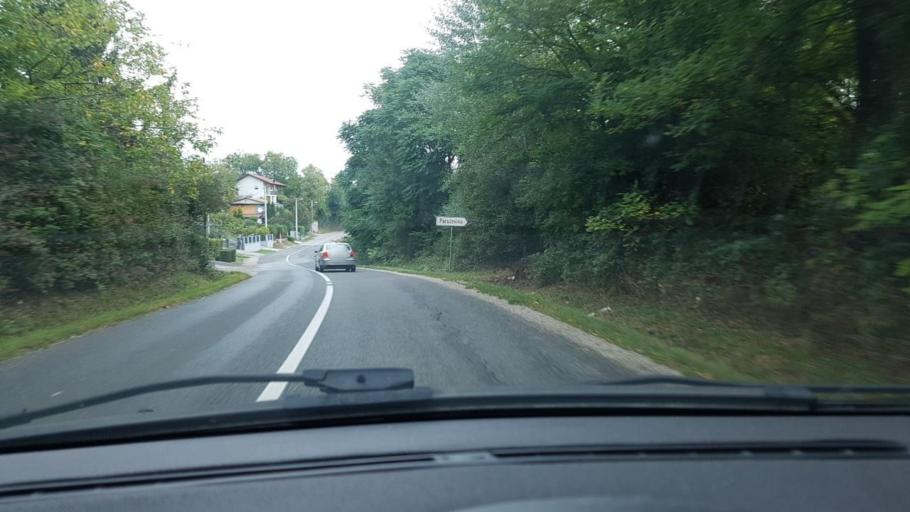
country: HR
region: Grad Zagreb
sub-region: Sesvete
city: Sesvete
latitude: 45.8939
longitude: 16.1249
